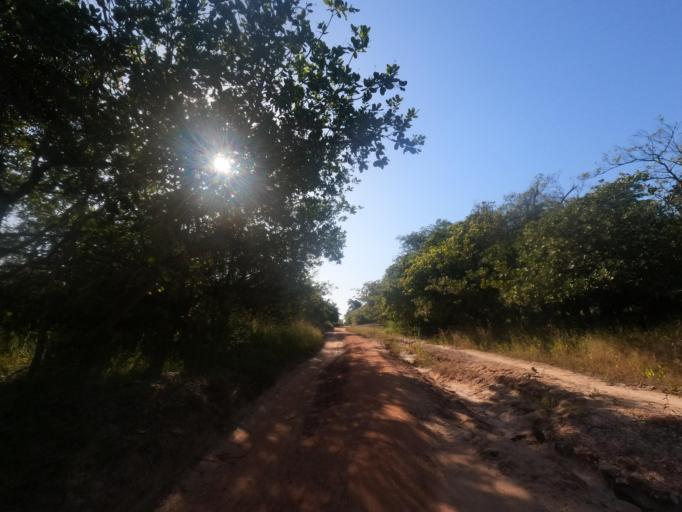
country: GW
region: Cacheu
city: Cacheu
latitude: 12.3935
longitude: -16.2391
